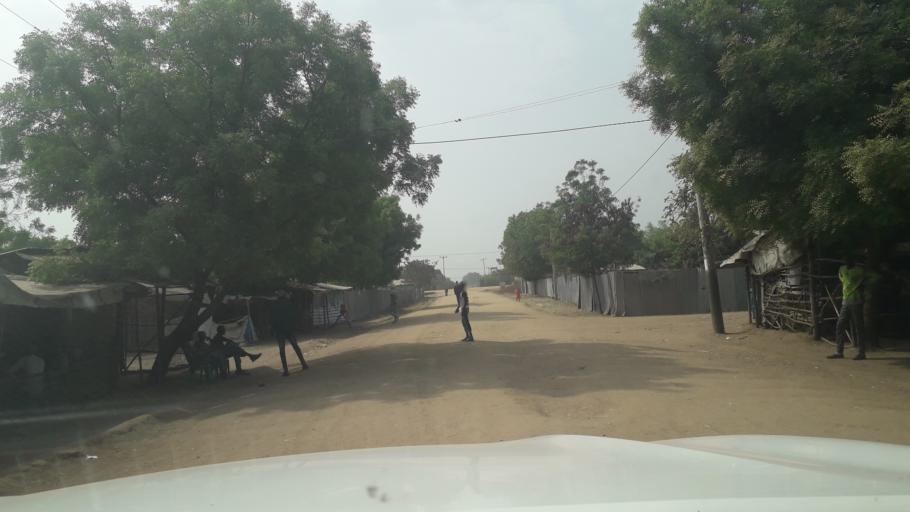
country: ET
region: Gambela
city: Gambela
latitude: 8.2996
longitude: 33.6829
